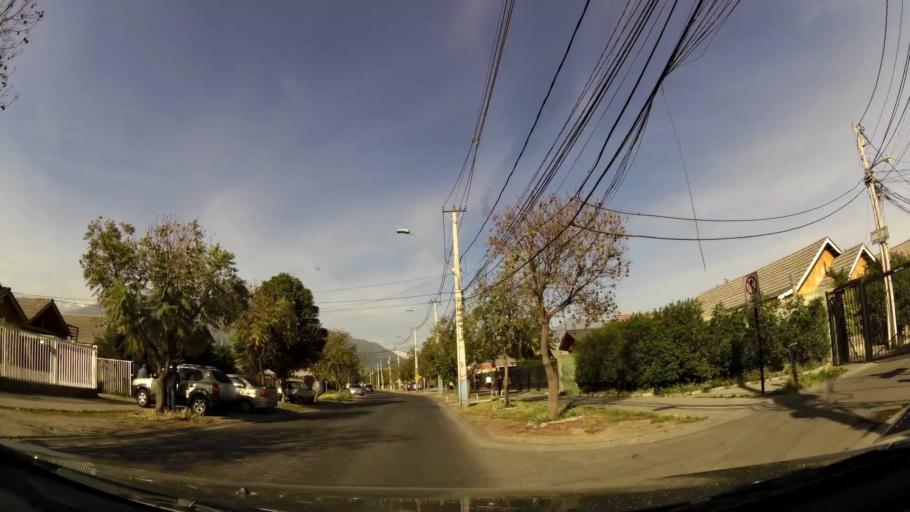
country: CL
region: Santiago Metropolitan
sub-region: Provincia de Cordillera
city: Puente Alto
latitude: -33.5853
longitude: -70.5627
